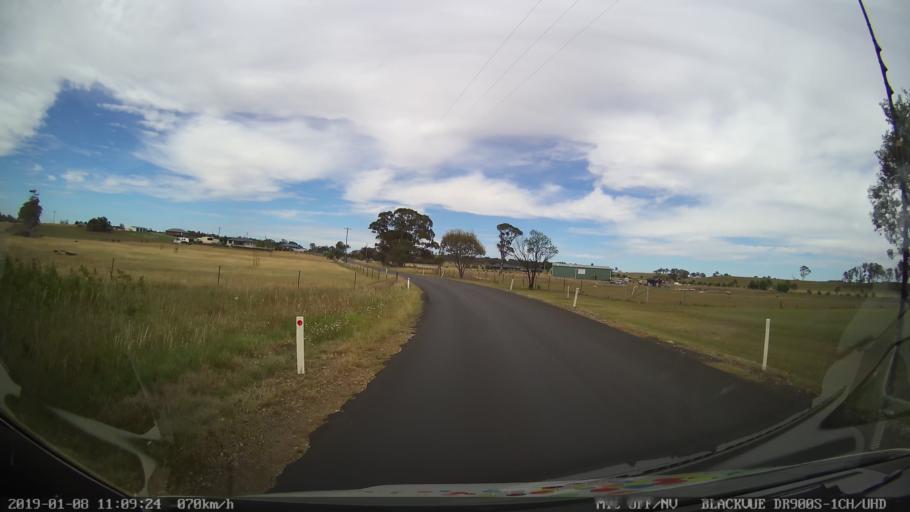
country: AU
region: New South Wales
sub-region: Guyra
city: Guyra
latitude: -30.2253
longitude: 151.6476
